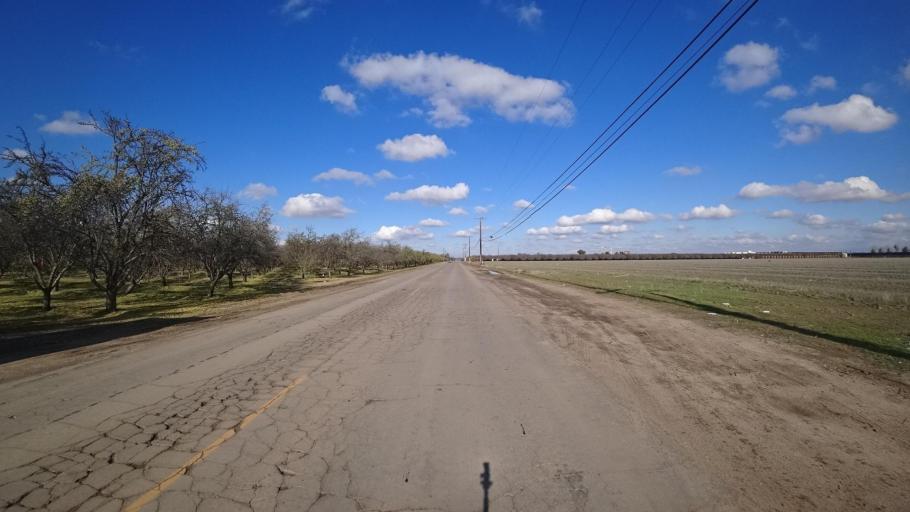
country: US
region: California
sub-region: Kern County
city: McFarland
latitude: 35.7077
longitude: -119.2408
